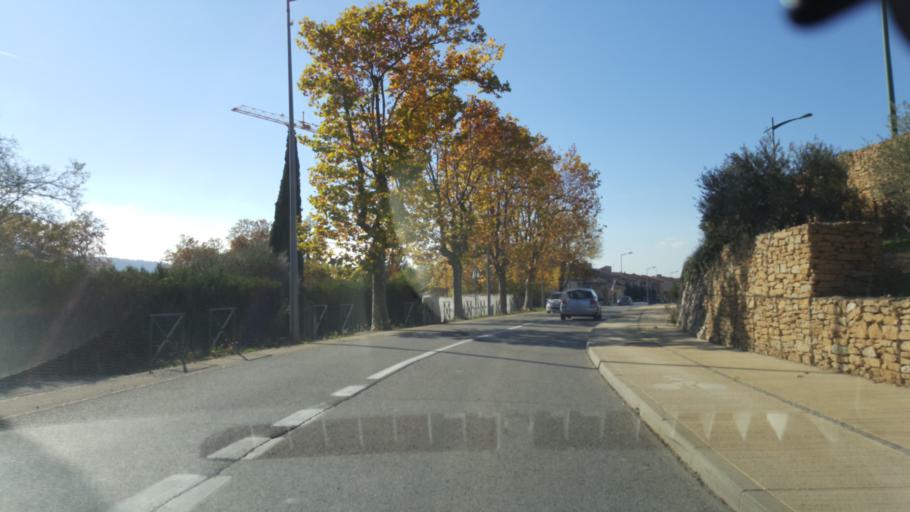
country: FR
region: Provence-Alpes-Cote d'Azur
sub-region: Departement du Var
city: Saint-Zacharie
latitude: 43.3856
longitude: 5.7139
